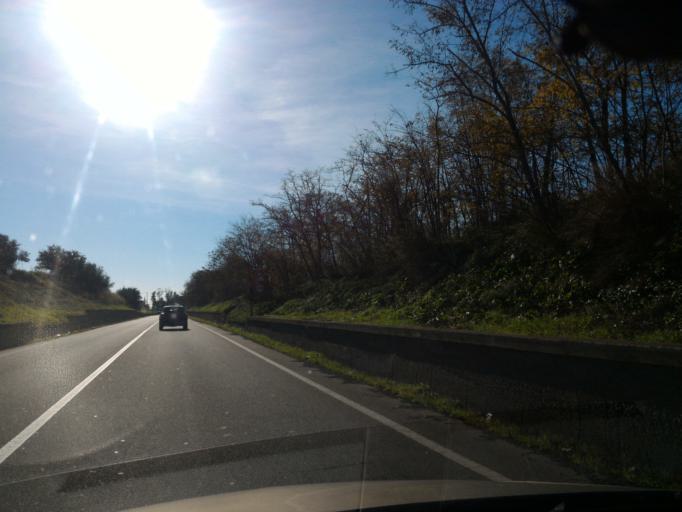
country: IT
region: Calabria
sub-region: Provincia di Crotone
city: Tronca
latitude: 39.2128
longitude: 17.1084
